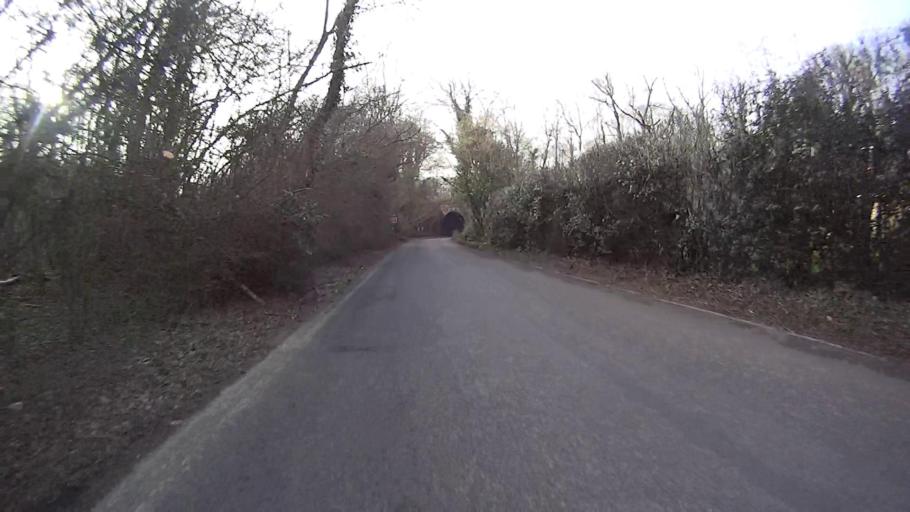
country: GB
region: England
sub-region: West Sussex
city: Crawley Down
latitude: 51.1167
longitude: -0.0928
